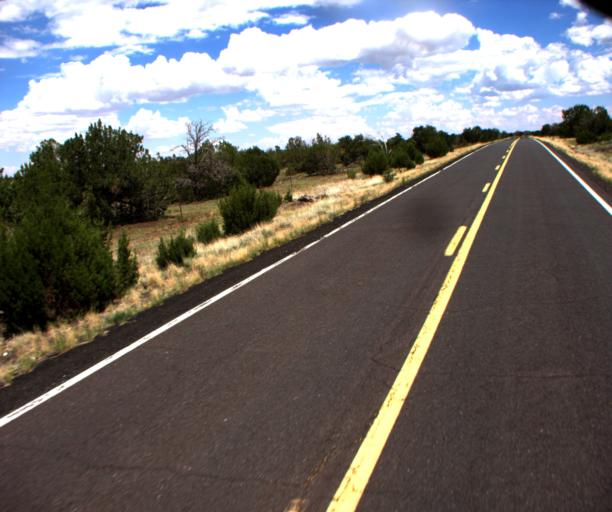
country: US
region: Arizona
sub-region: Coconino County
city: Parks
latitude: 35.5642
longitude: -111.8927
